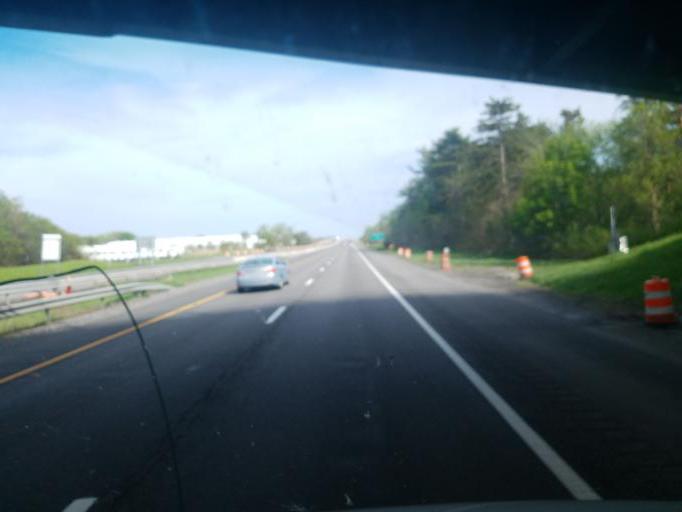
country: US
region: New York
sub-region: Onondaga County
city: Liverpool
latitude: 43.1125
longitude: -76.2057
